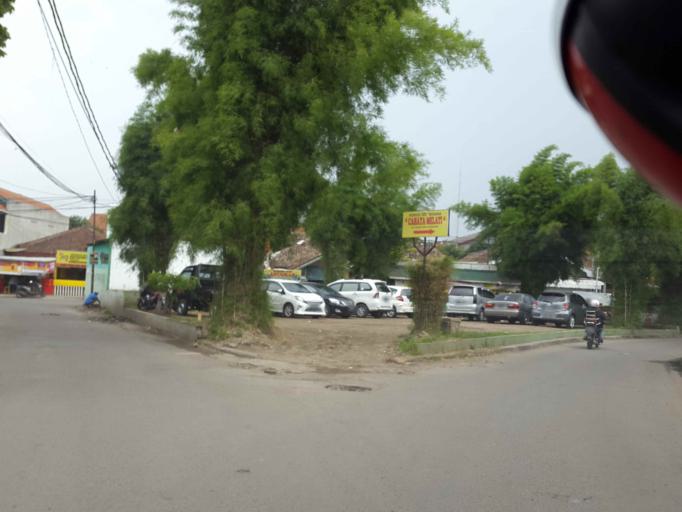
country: ID
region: West Java
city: Cimahi
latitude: -6.8831
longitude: 107.5326
